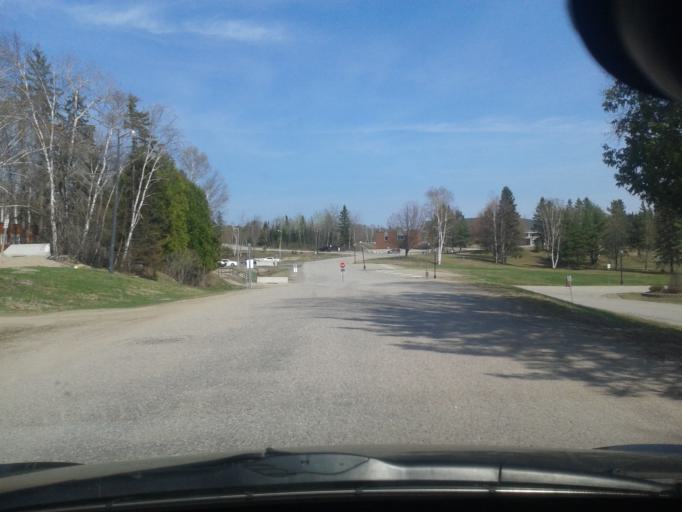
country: CA
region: Ontario
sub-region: Nipissing District
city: North Bay
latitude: 46.3454
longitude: -79.4937
